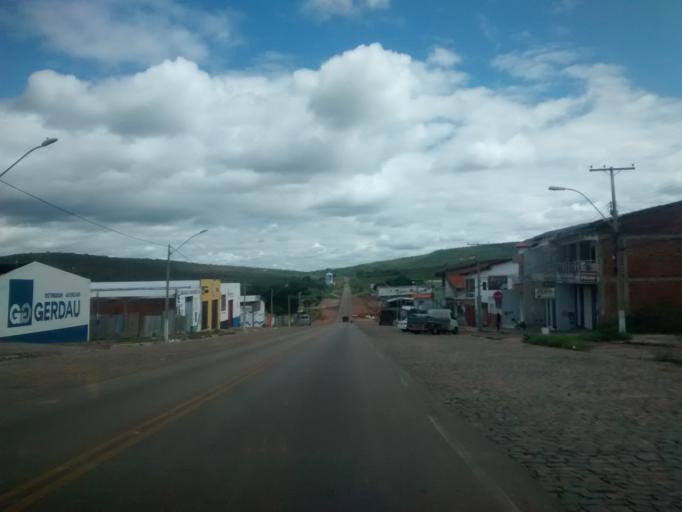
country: BR
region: Bahia
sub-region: Brumado
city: Brumado
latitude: -14.2174
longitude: -41.6842
